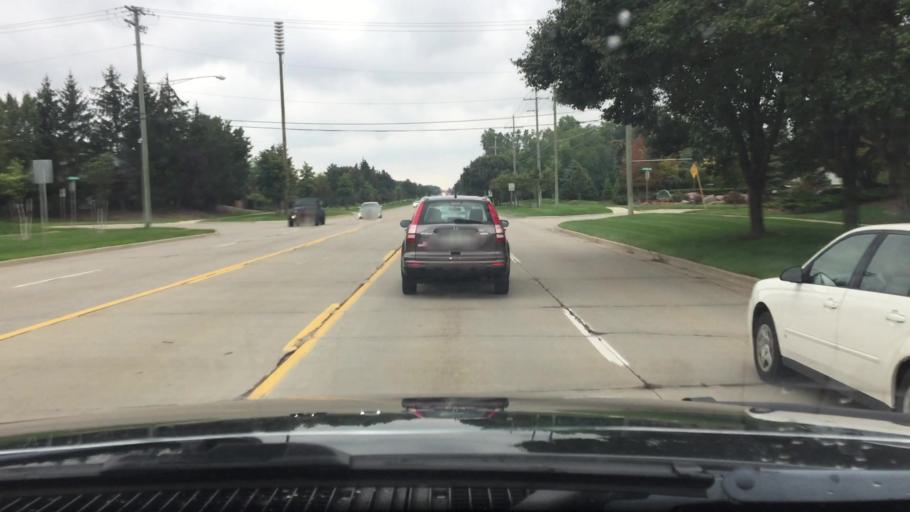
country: US
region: Michigan
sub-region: Macomb County
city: Utica
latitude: 42.6160
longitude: -83.0716
